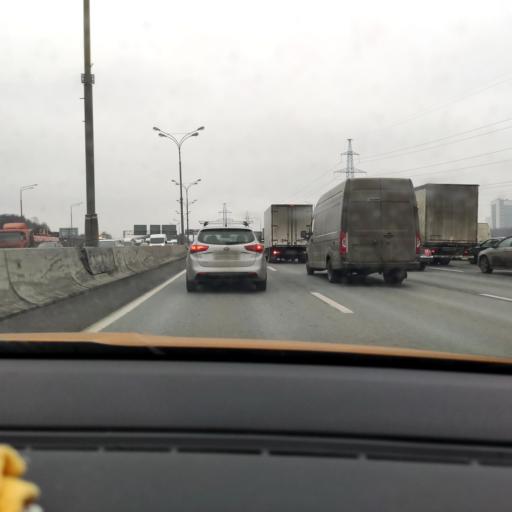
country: RU
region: Moscow
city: Tyoply Stan
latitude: 55.6017
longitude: 37.4982
